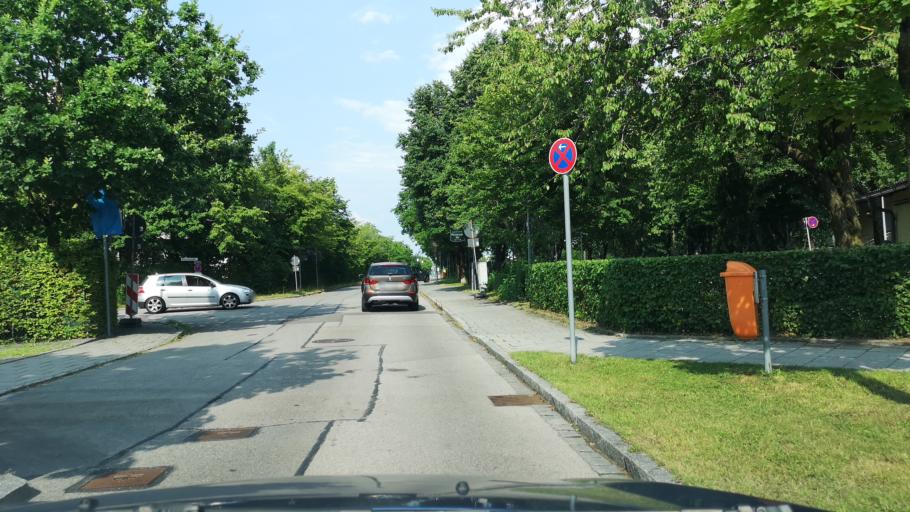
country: DE
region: Bavaria
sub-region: Upper Bavaria
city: Kirchheim bei Muenchen
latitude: 48.1746
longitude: 11.7613
